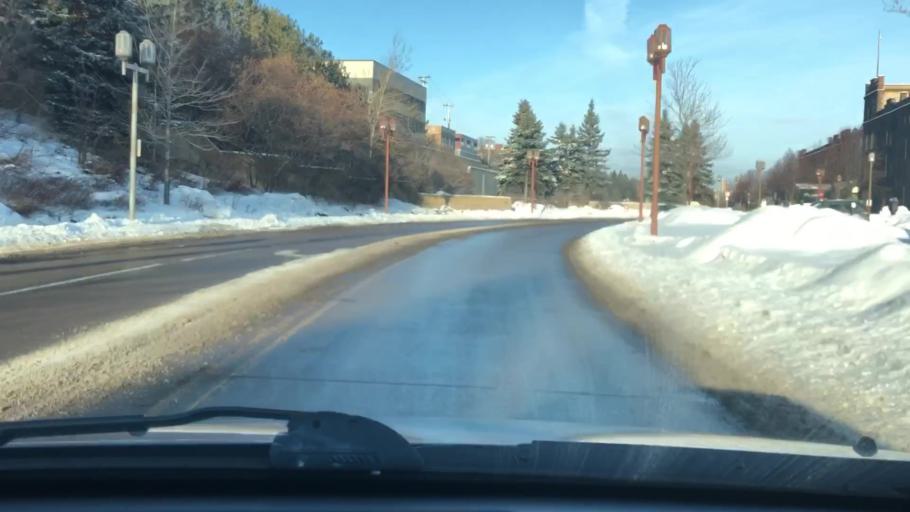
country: US
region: Minnesota
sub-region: Saint Louis County
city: Duluth
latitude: 46.7917
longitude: -92.0923
